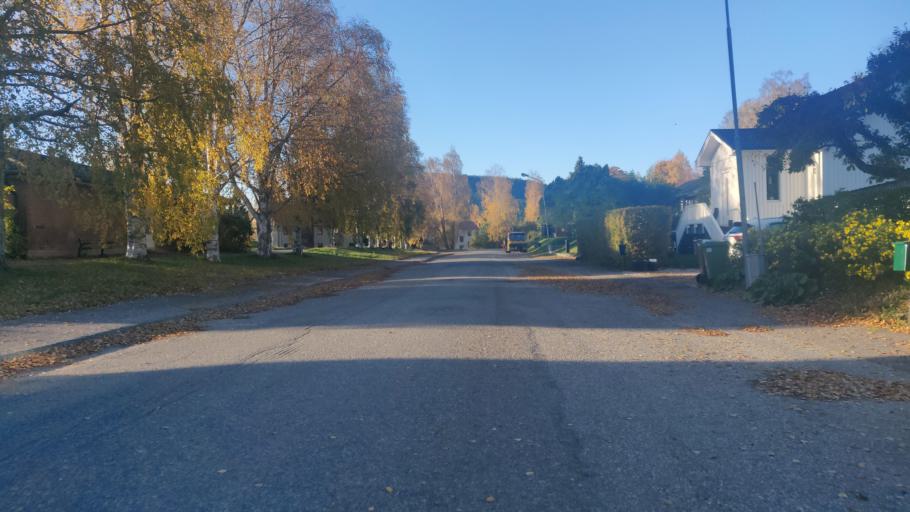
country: SE
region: Vaesternorrland
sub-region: Sundsvalls Kommun
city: Skottsund
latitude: 62.2911
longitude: 17.3900
